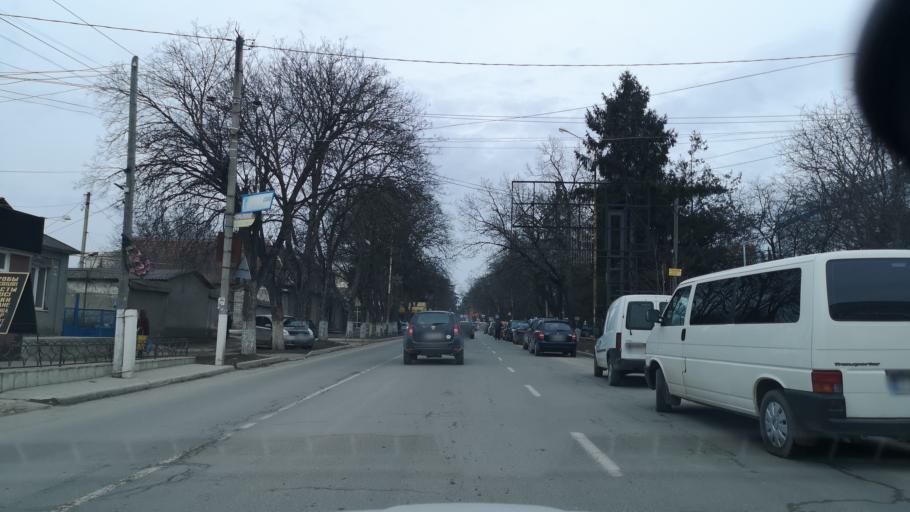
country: MD
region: Raionul Edinet
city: Edinet
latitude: 48.1670
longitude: 27.3097
